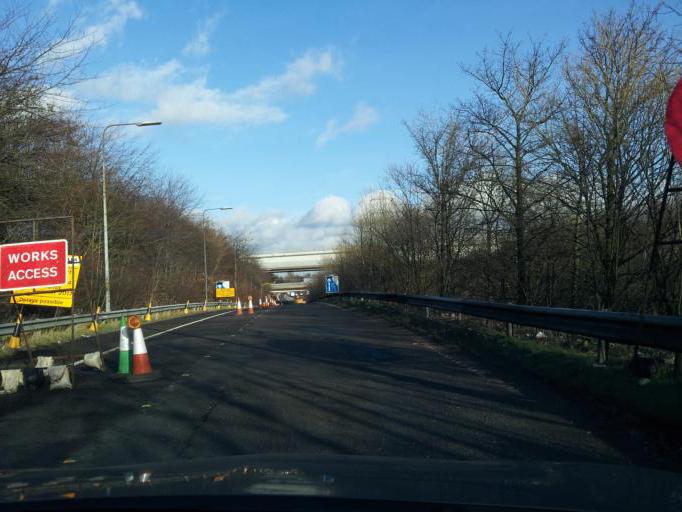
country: GB
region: England
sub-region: Borough of Bury
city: Prestwich
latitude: 53.5397
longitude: -2.2882
